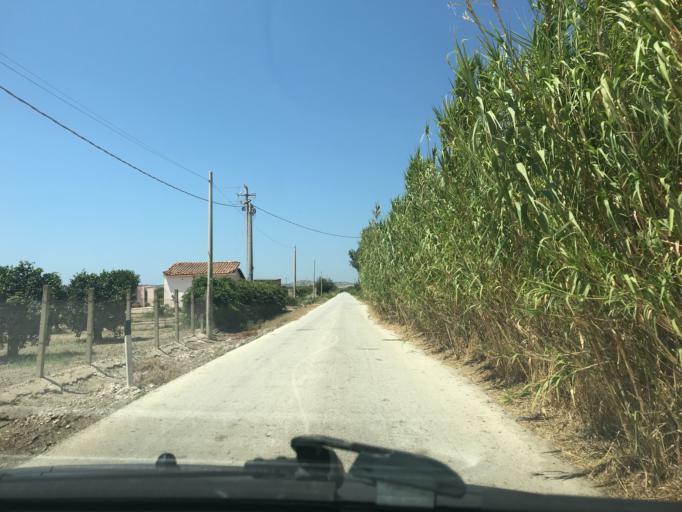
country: IT
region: Sicily
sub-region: Provincia di Siracusa
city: Noto
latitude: 36.8349
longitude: 15.0500
